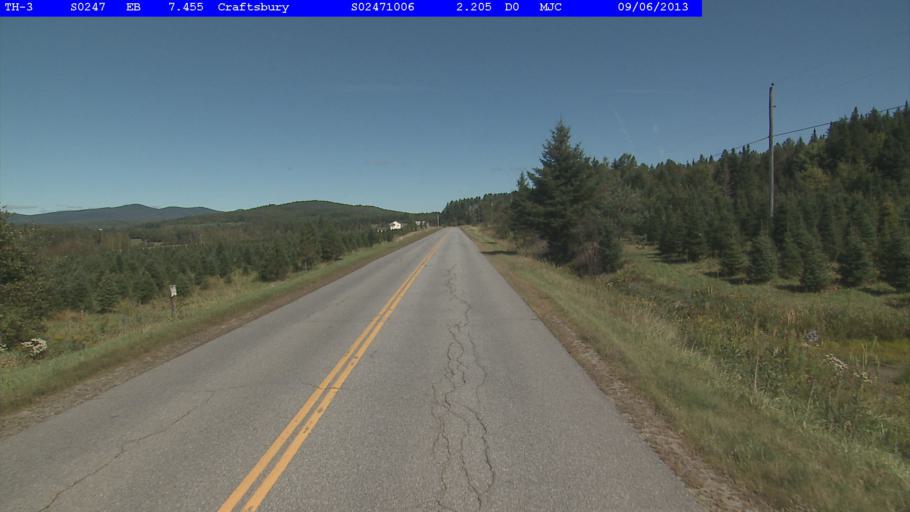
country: US
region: Vermont
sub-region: Caledonia County
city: Hardwick
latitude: 44.6431
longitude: -72.4185
